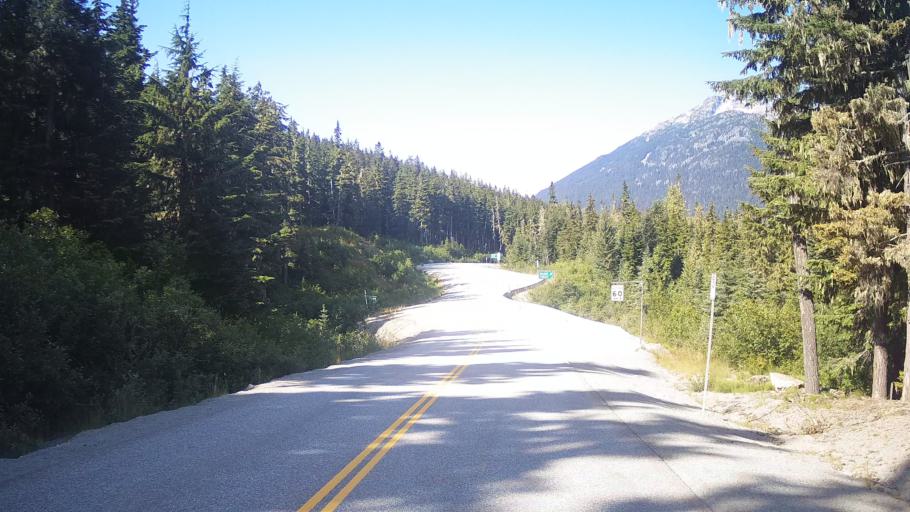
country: CA
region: British Columbia
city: Pemberton
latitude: 50.3681
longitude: -122.5040
